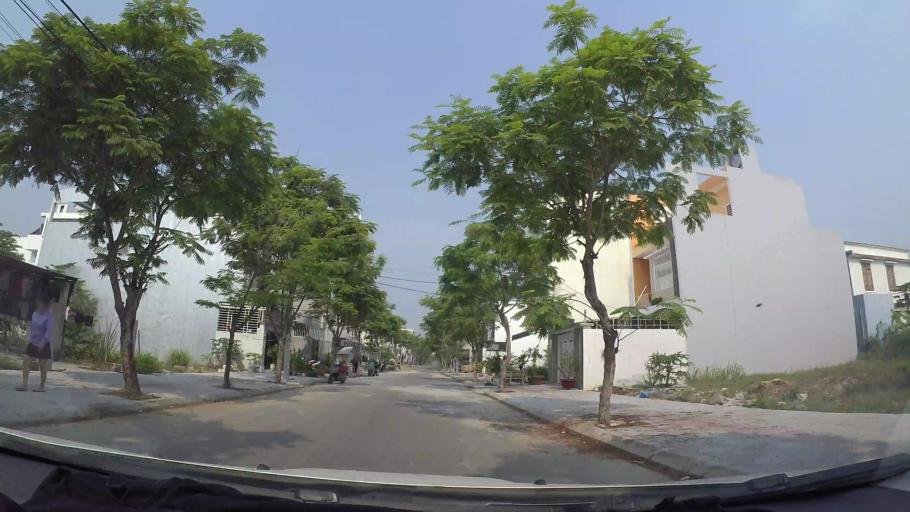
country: VN
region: Da Nang
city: Cam Le
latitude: 16.0036
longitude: 108.2224
